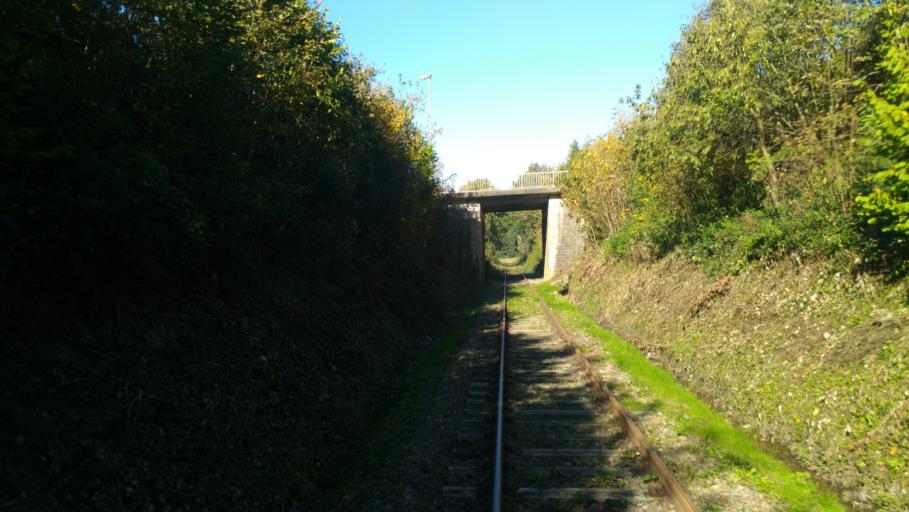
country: DE
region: Lower Saxony
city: Buchholz
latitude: 52.2243
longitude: 9.1223
